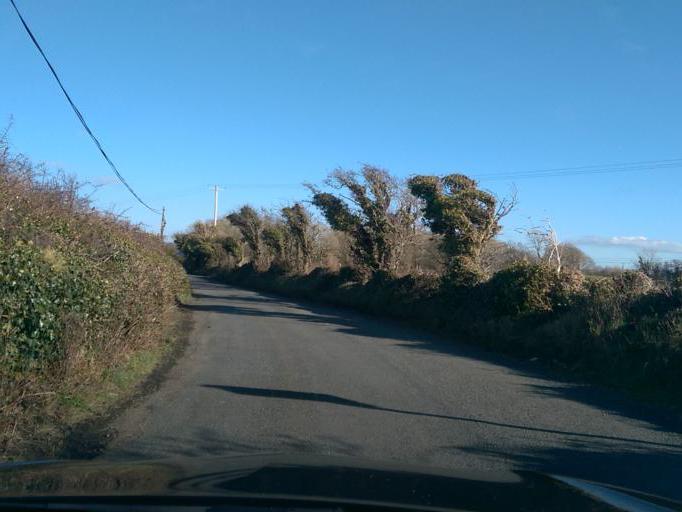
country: IE
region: Connaught
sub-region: County Galway
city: Oranmore
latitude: 53.2331
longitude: -8.9612
